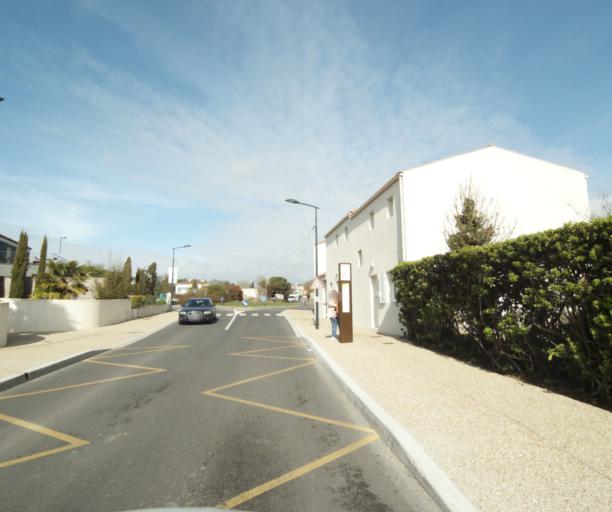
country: FR
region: Poitou-Charentes
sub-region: Departement de la Charente-Maritime
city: La Rochelle
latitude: 46.1758
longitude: -1.1595
